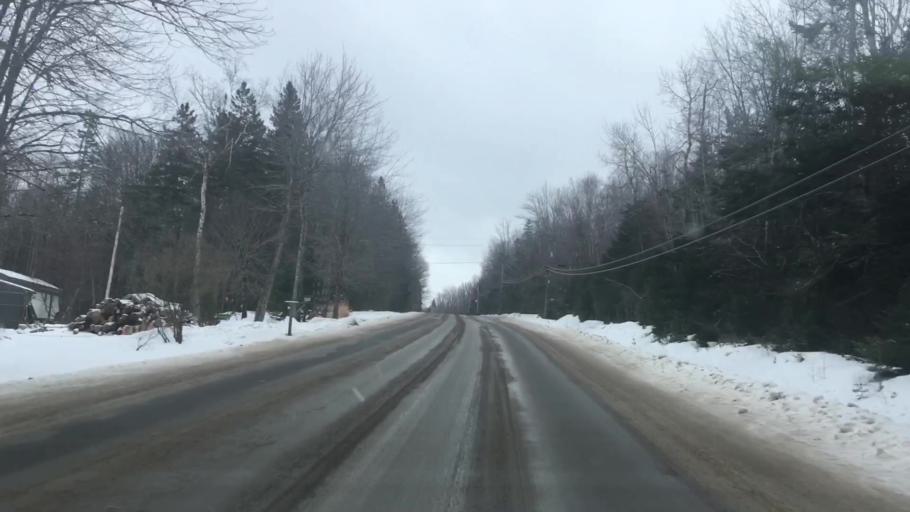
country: US
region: Maine
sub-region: Washington County
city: East Machias
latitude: 44.9896
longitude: -67.4599
